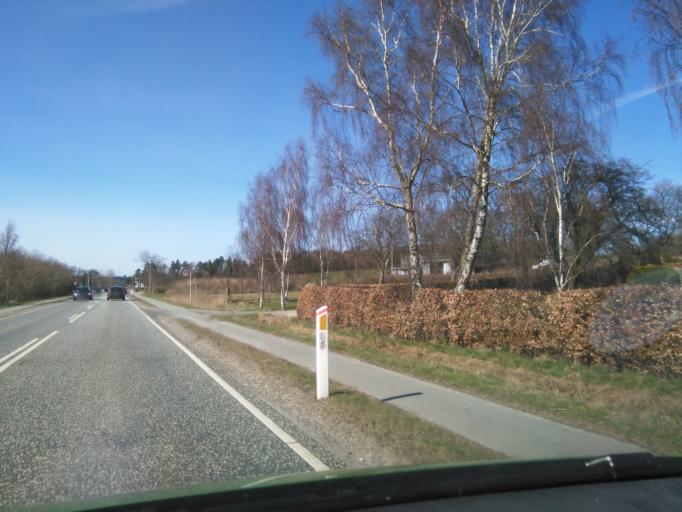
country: DK
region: Central Jutland
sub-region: Favrskov Kommune
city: Soften
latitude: 56.2426
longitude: 10.0805
